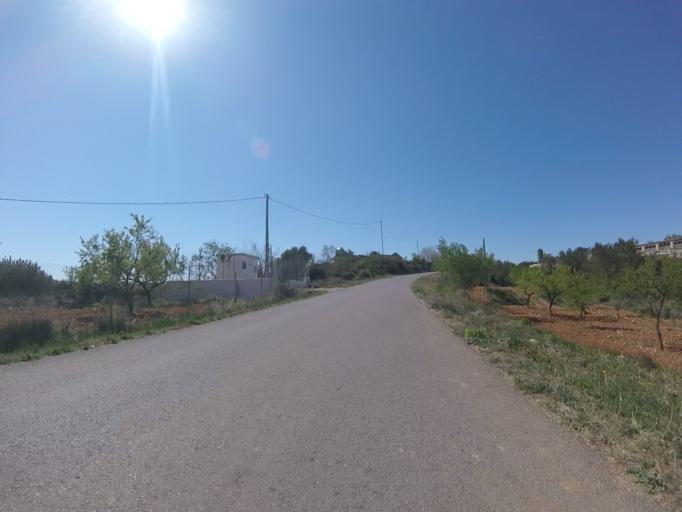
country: ES
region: Valencia
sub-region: Provincia de Castello
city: Cuevas de Vinroma
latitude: 40.3793
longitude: 0.1369
